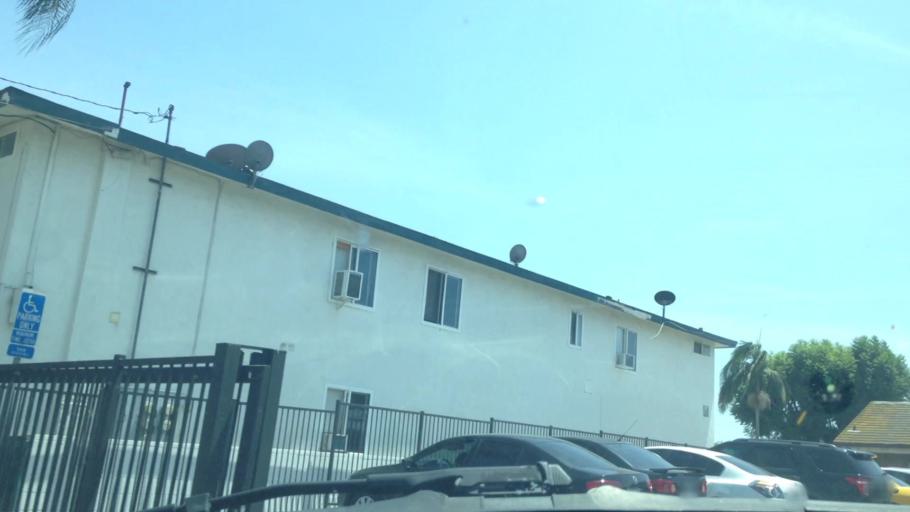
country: US
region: California
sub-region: Los Angeles County
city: Downey
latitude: 33.9317
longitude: -118.1457
